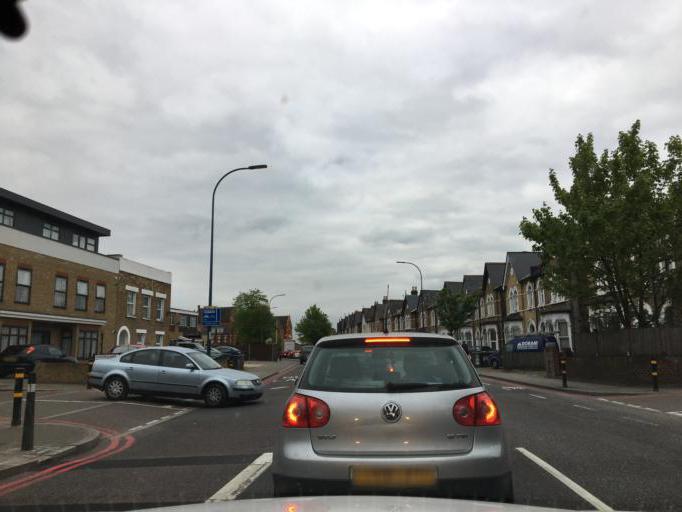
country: GB
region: England
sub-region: Greater London
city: Catford
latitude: 51.4421
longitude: -0.0315
